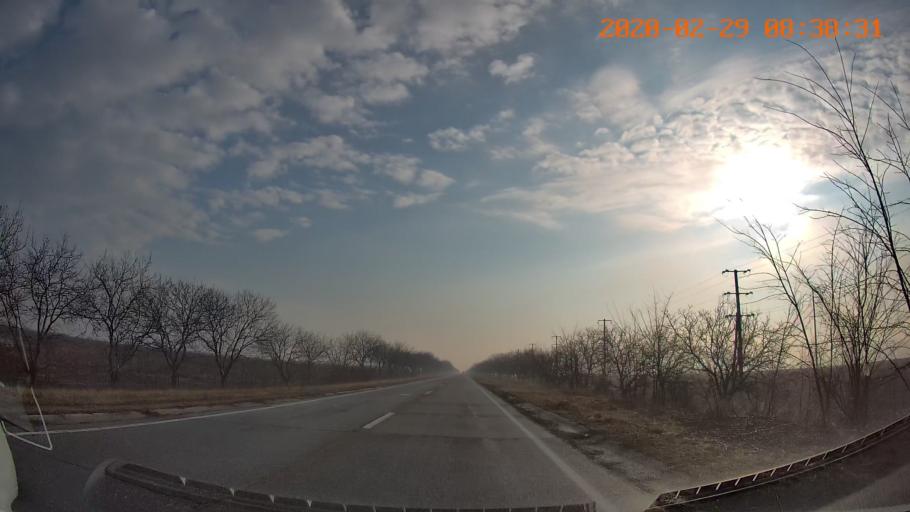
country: MD
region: Anenii Noi
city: Varnita
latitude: 46.9218
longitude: 29.3802
